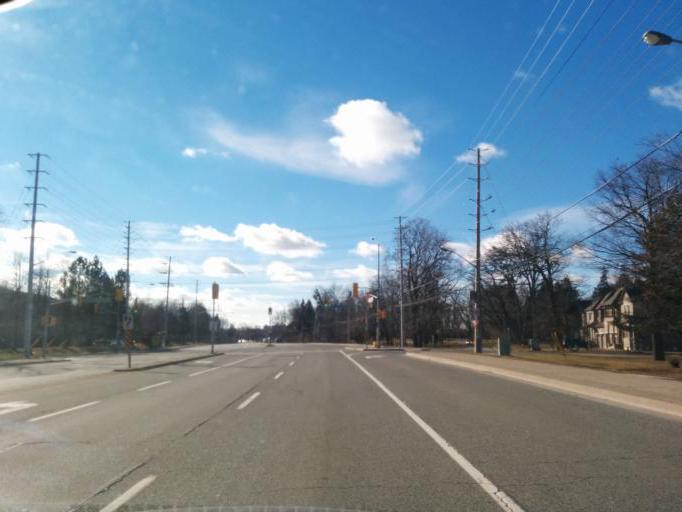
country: CA
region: Ontario
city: Mississauga
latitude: 43.5524
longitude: -79.6484
